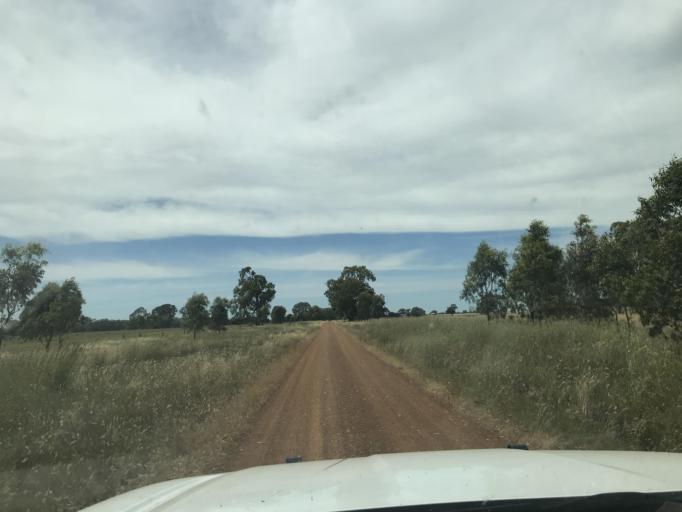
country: AU
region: South Australia
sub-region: Wattle Range
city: Penola
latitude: -37.0212
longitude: 141.4849
